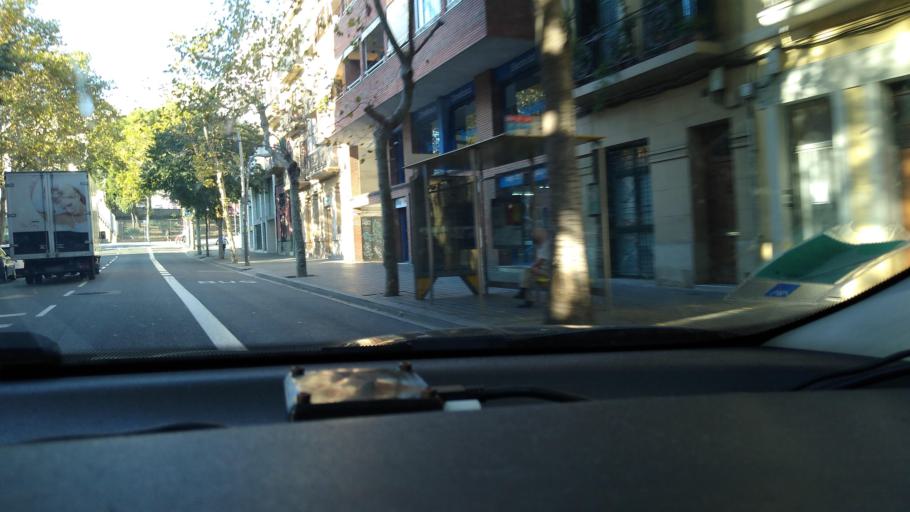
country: ES
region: Catalonia
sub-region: Provincia de Barcelona
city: les Corts
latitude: 41.3784
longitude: 2.1237
